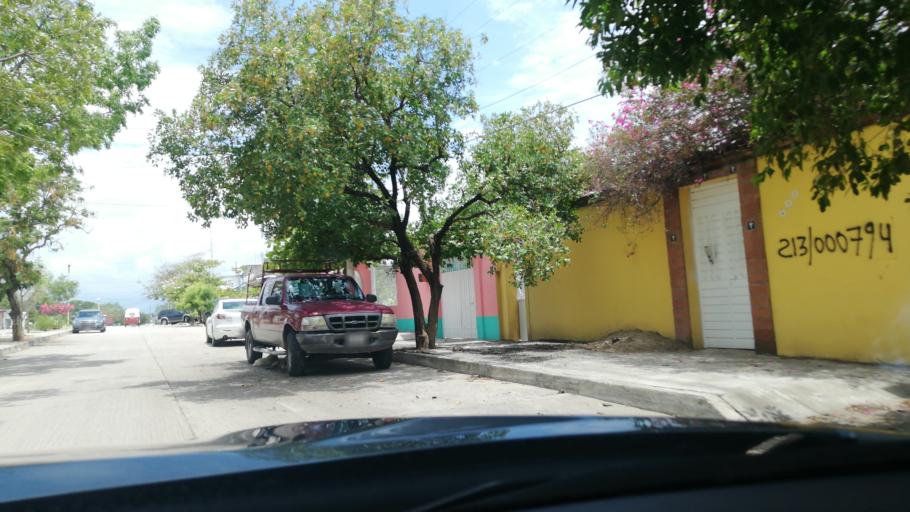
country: MX
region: Oaxaca
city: Santa Maria Jalapa del Marques
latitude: 16.4401
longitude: -95.4400
